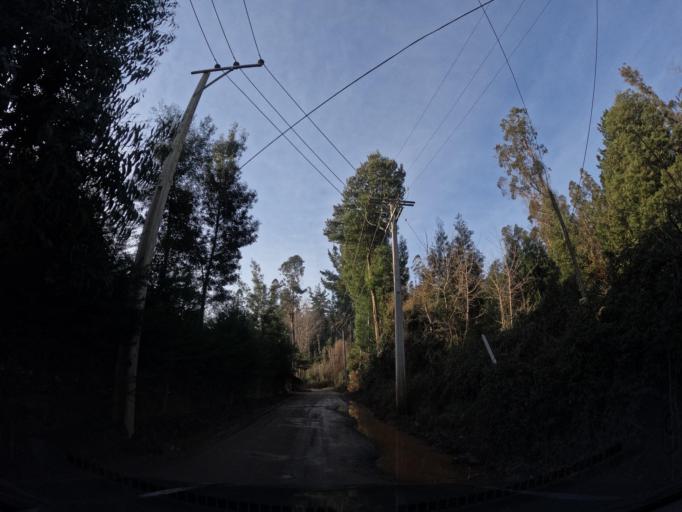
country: CL
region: Biobio
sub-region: Provincia de Concepcion
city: Concepcion
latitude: -36.8614
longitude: -72.9976
